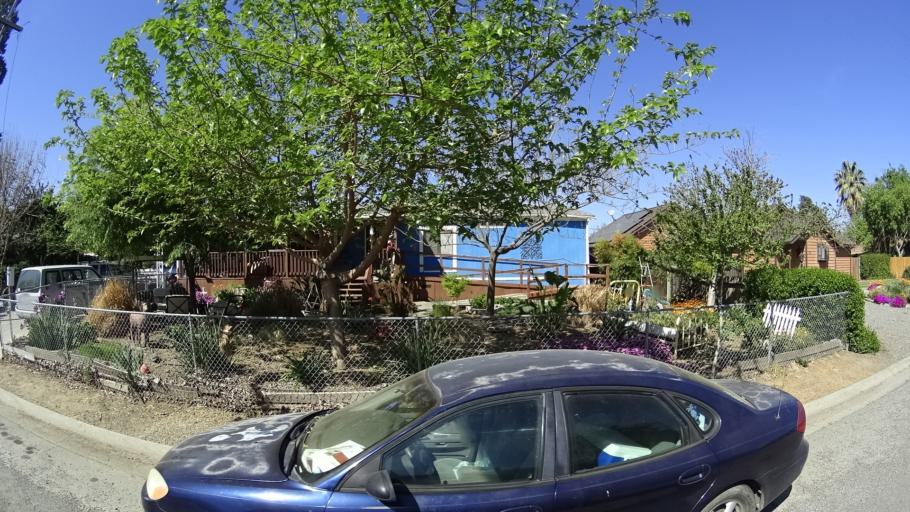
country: US
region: California
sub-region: Glenn County
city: Willows
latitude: 39.5272
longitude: -122.1896
